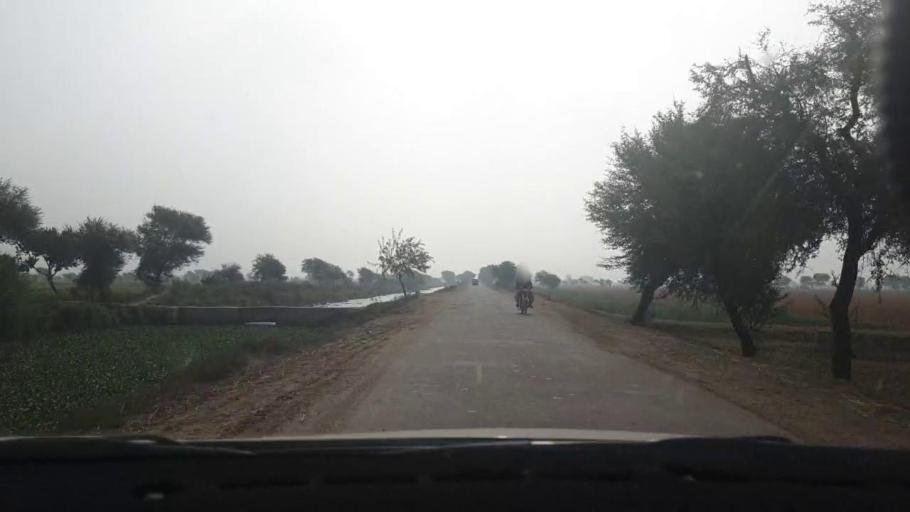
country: PK
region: Sindh
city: Tando Muhammad Khan
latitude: 25.0685
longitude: 68.5390
